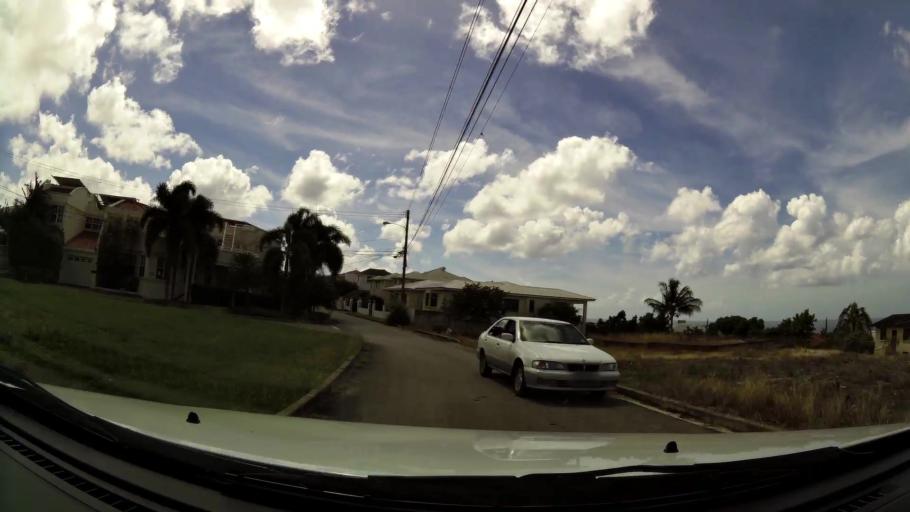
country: BB
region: Saint James
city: Holetown
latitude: 13.1443
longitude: -59.6289
